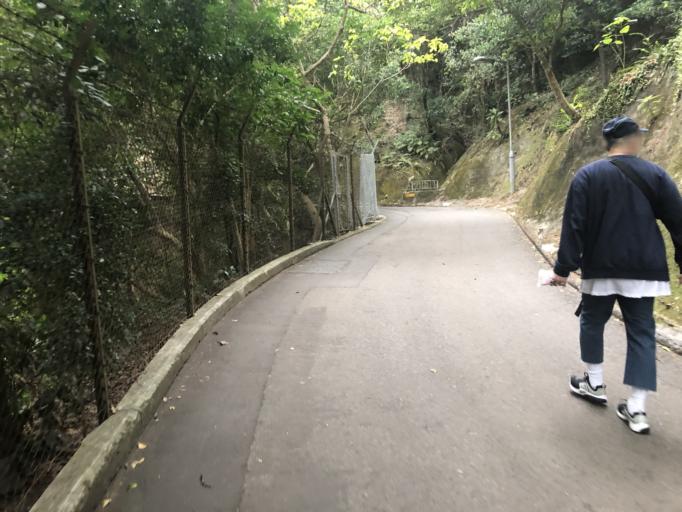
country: HK
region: Wanchai
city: Wan Chai
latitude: 22.2827
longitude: 114.2122
